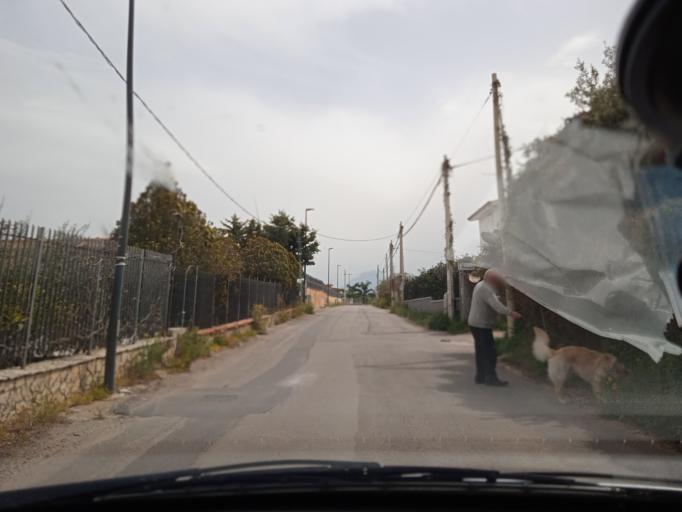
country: IT
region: Sicily
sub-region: Palermo
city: Torre Colonna-Sperone
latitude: 38.0302
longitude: 13.5687
